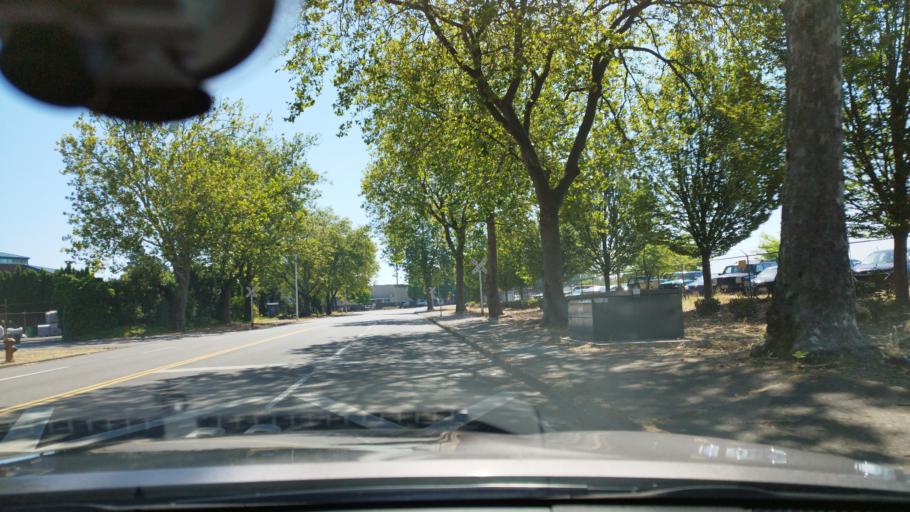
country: US
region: Oregon
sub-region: Multnomah County
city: Portland
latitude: 45.5628
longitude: -122.7177
